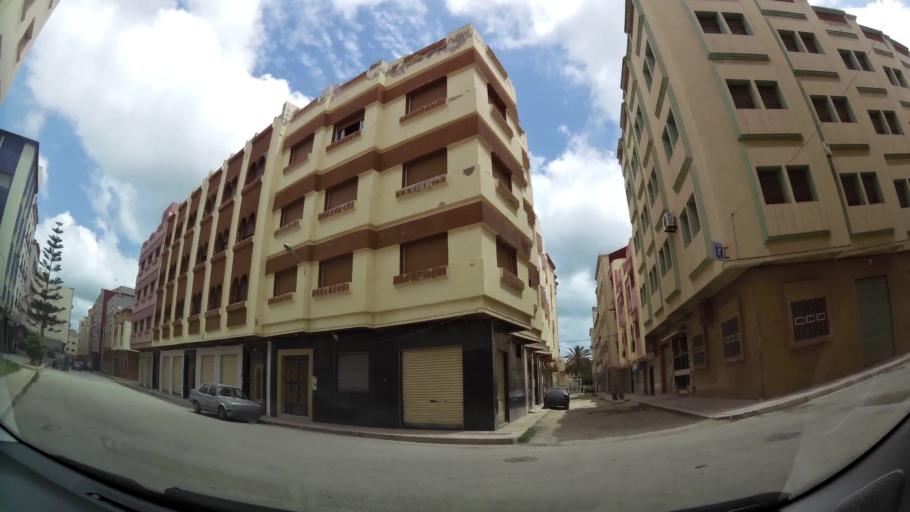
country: MA
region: Oriental
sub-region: Nador
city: Nador
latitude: 35.1669
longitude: -2.9224
